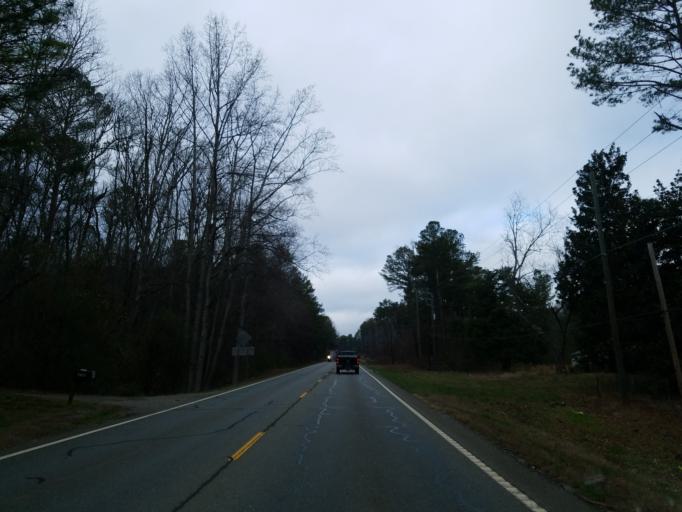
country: US
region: Georgia
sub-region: Cherokee County
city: Canton
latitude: 34.2780
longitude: -84.5082
